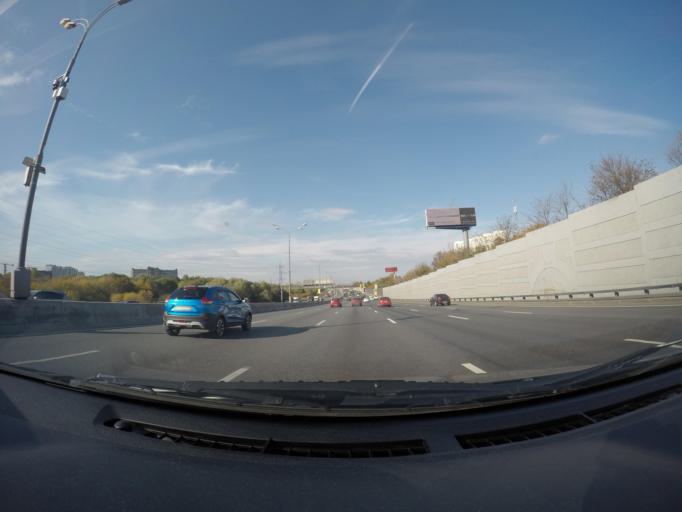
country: RU
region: Moscow
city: Yaroslavskiy
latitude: 55.8878
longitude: 37.7154
